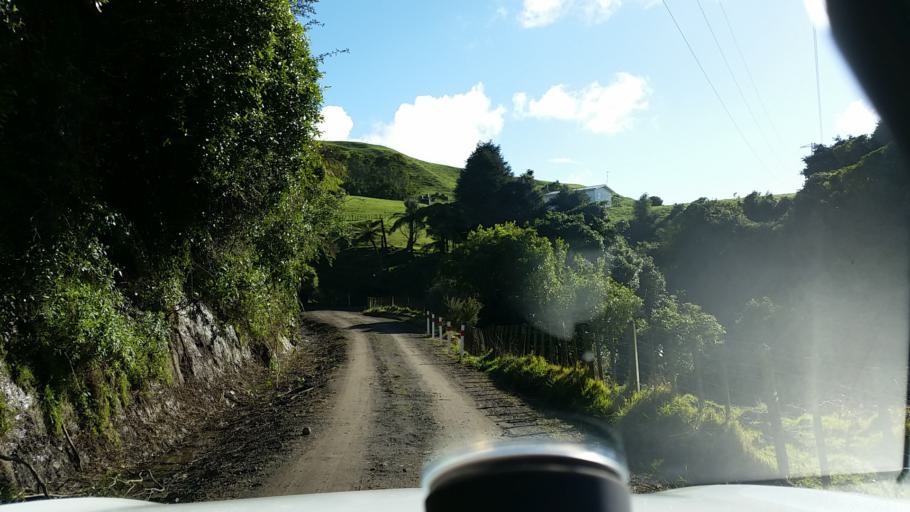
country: NZ
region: Taranaki
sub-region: South Taranaki District
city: Eltham
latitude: -39.4592
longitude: 174.3695
